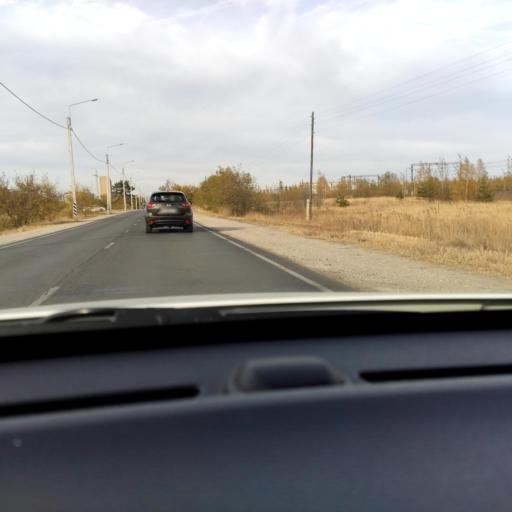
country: RU
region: Voronezj
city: Maslovka
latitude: 51.5816
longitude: 39.2475
